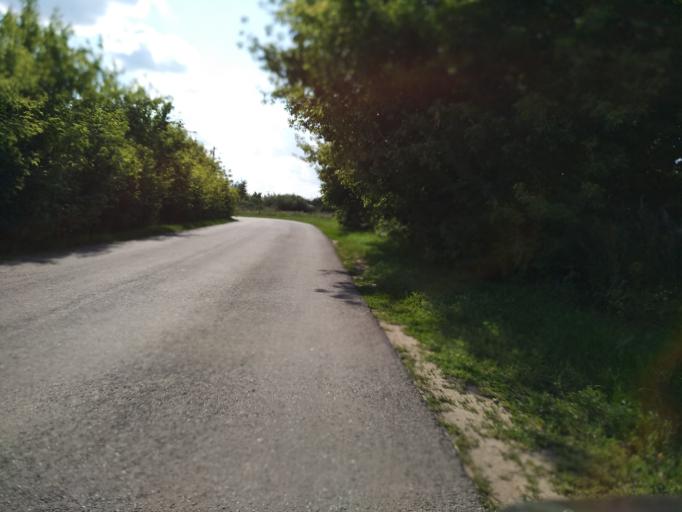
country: RU
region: Lipetsk
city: Dobrinka
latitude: 52.0407
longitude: 40.5524
